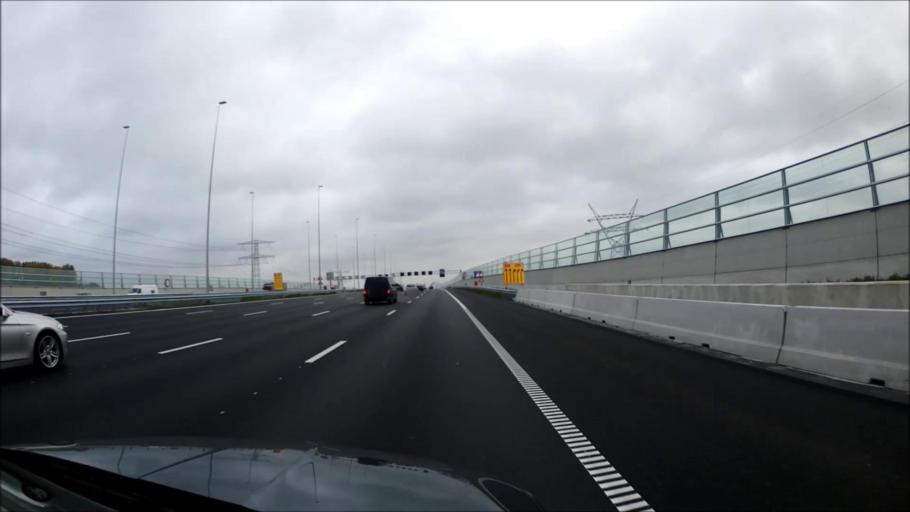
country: NL
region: North Holland
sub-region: Gemeente Weesp
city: Weesp
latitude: 52.3227
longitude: 5.0674
